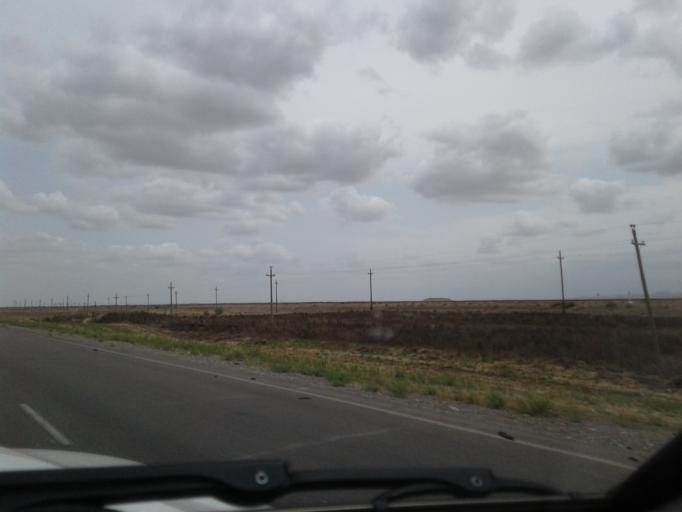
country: IR
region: Razavi Khorasan
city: Dargaz
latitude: 37.5912
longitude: 59.2406
